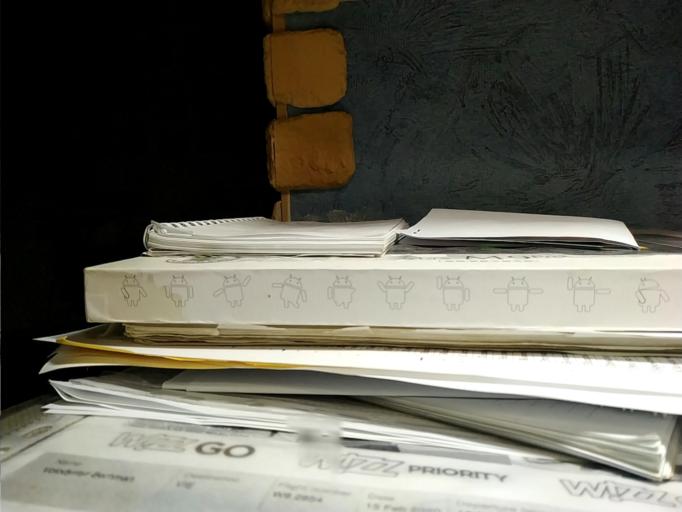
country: RU
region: Arkhangelskaya
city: Konevo
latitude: 62.7350
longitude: 38.5962
